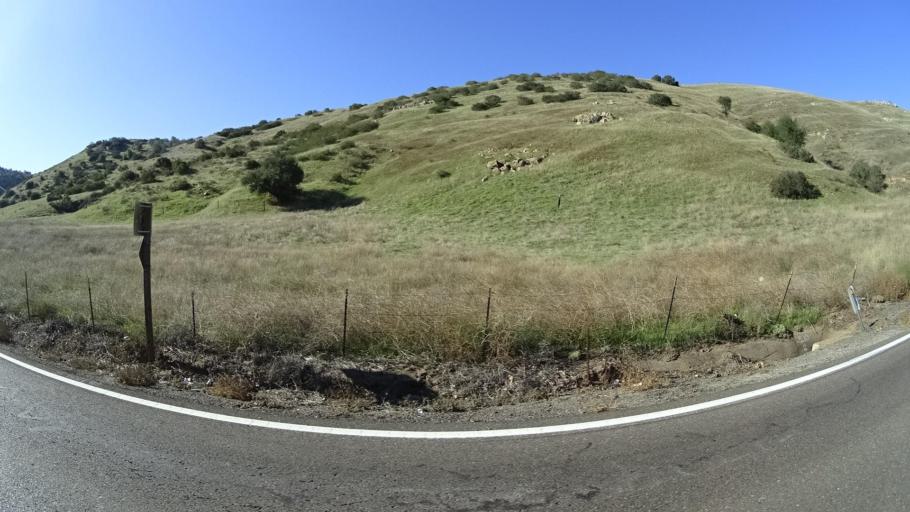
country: US
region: California
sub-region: San Diego County
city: Jamul
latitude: 32.6644
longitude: -116.8203
